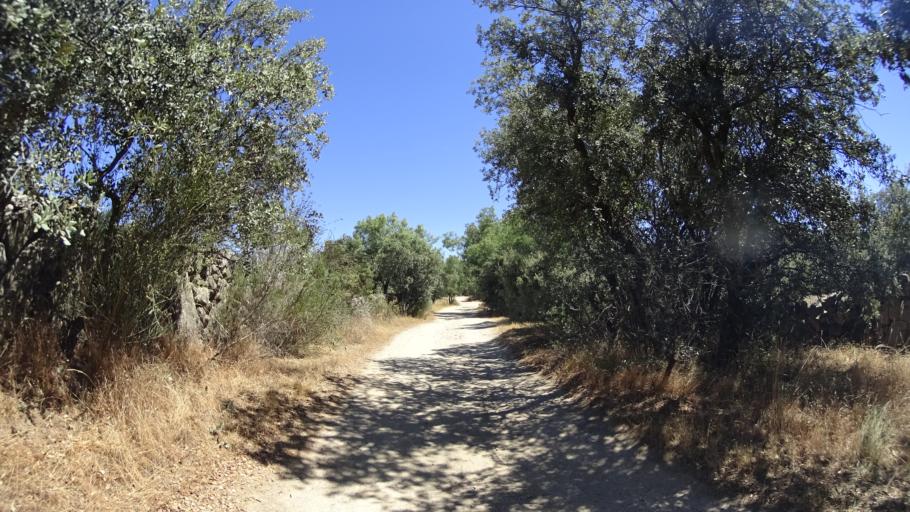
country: ES
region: Madrid
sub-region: Provincia de Madrid
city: Alpedrete
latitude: 40.6726
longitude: -4.0411
